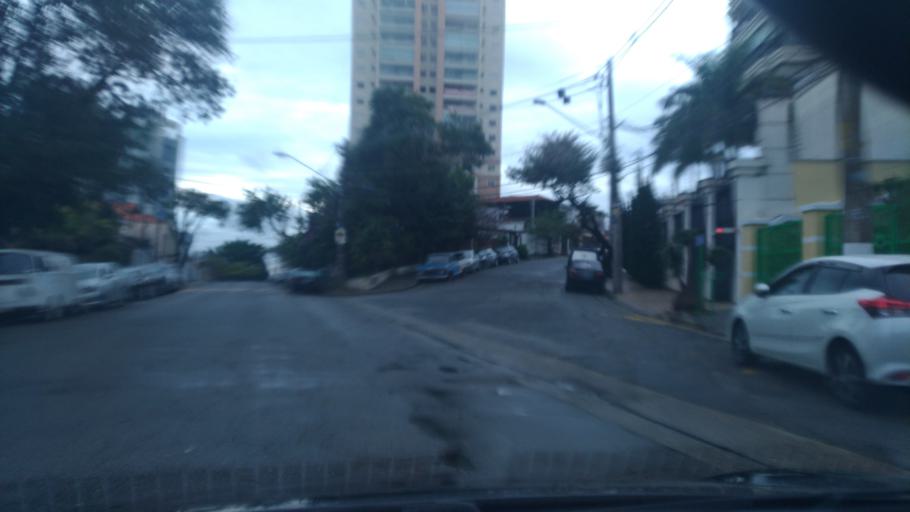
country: BR
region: Sao Paulo
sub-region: Sao Paulo
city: Sao Paulo
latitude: -23.5118
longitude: -46.5820
